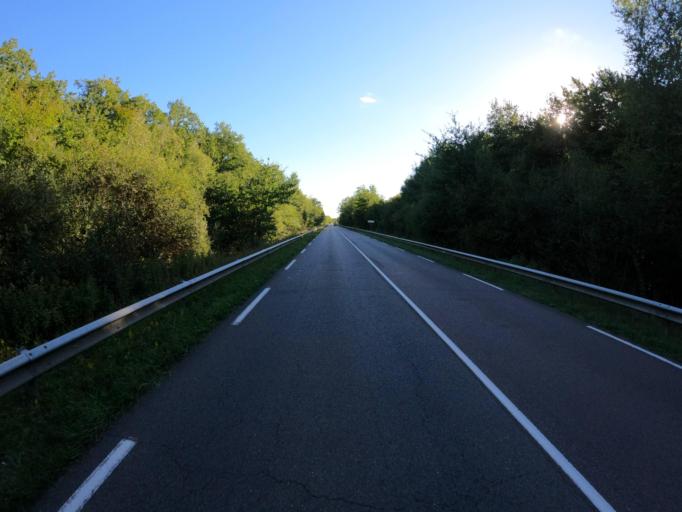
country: FR
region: Bourgogne
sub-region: Departement de Saone-et-Loire
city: Saint-Eusebe
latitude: 46.7277
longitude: 4.4360
